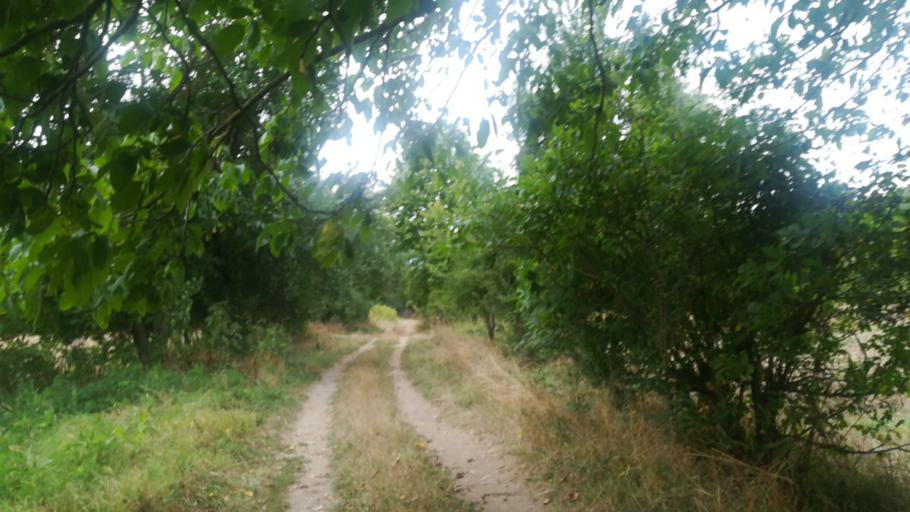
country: MK
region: Debarca
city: Belcista
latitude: 41.2854
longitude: 20.8296
